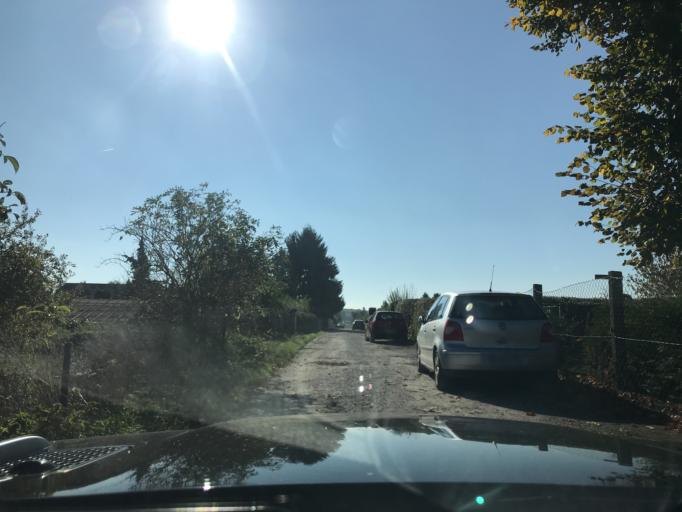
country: DE
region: Thuringia
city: Muehlhausen
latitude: 51.2240
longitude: 10.4448
